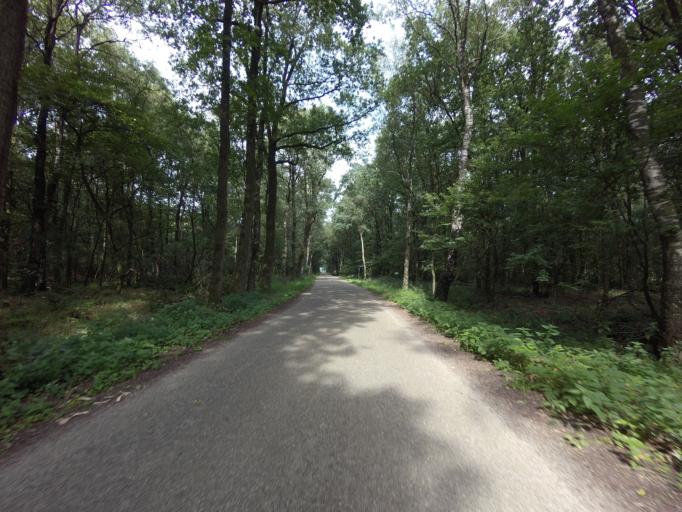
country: NL
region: Drenthe
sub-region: Gemeente Westerveld
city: Dwingeloo
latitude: 52.7911
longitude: 6.4339
